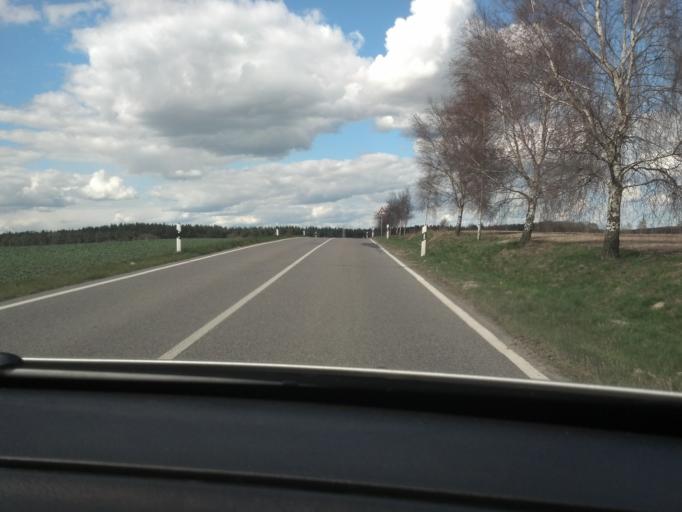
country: DE
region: Mecklenburg-Vorpommern
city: Burg Stargard
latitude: 53.5109
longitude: 13.3187
